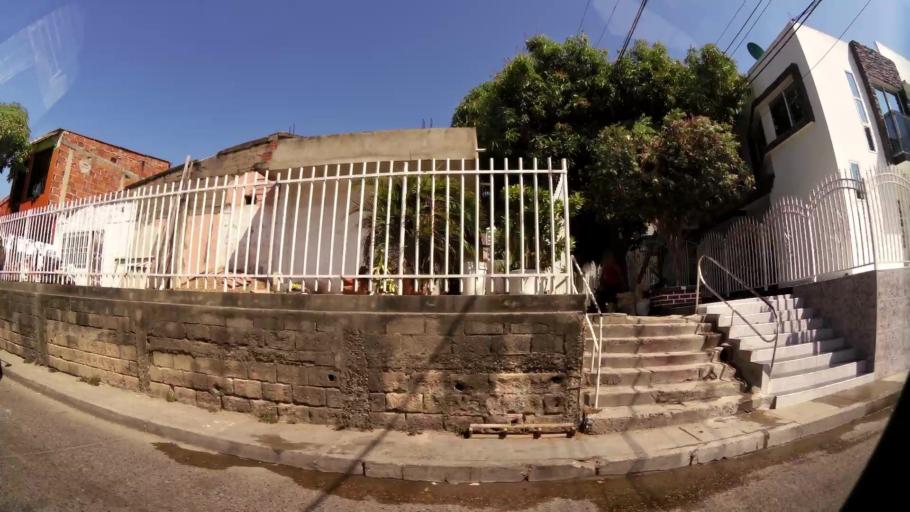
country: CO
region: Bolivar
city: Cartagena
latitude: 10.3892
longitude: -75.5099
